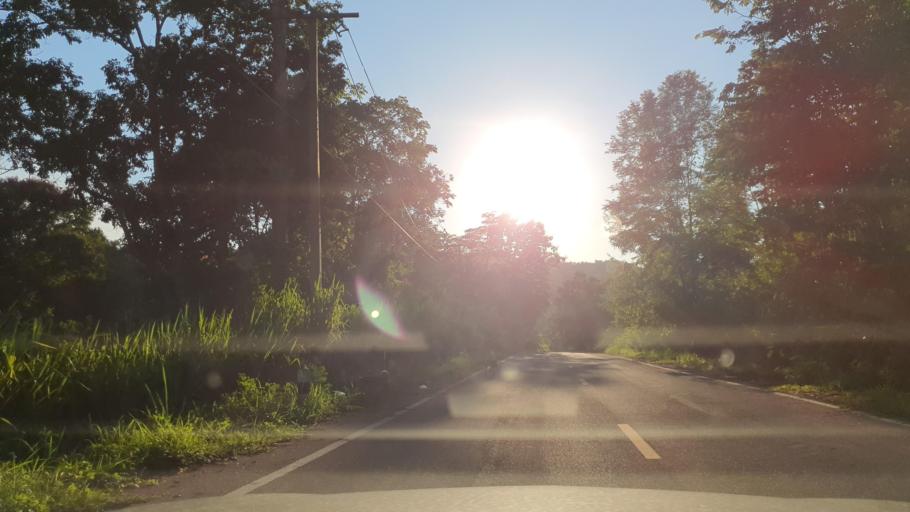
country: TH
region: Chiang Mai
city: Mae On
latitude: 18.8239
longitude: 99.2903
